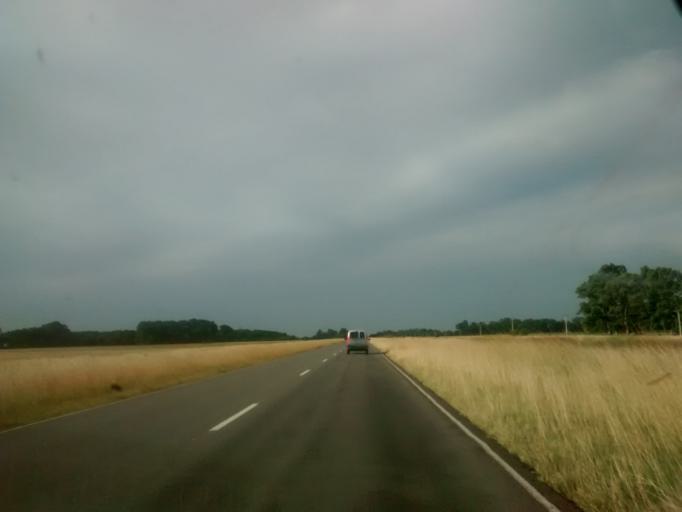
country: AR
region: Buenos Aires
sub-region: Partido de Ayacucho
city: Ayacucho
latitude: -36.6658
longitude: -58.5743
